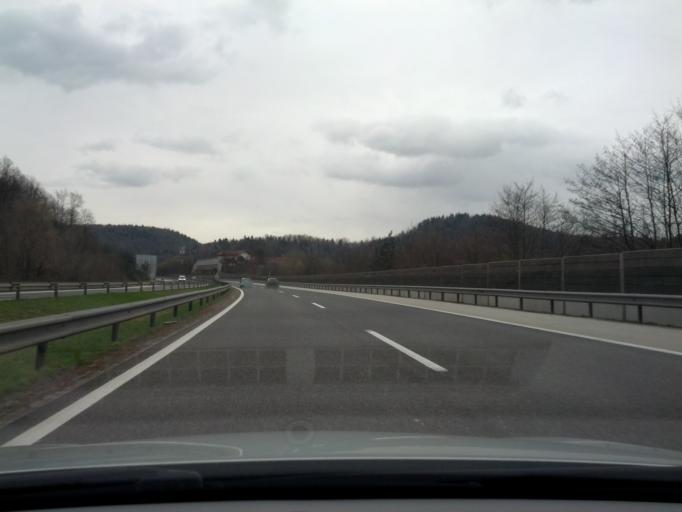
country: SI
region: Skofljica
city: Lavrica
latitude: 46.0058
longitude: 14.5695
